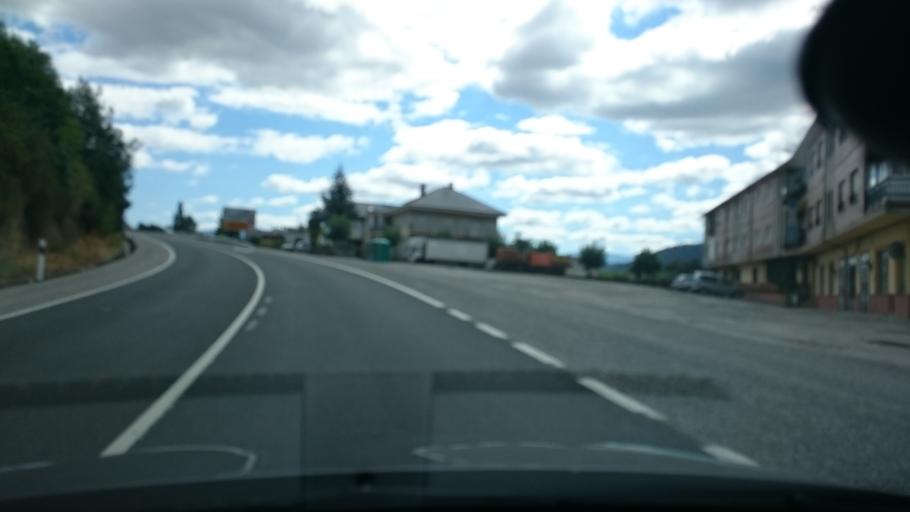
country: ES
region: Castille and Leon
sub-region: Provincia de Leon
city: Villafranca del Bierzo
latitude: 42.6037
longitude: -6.8147
